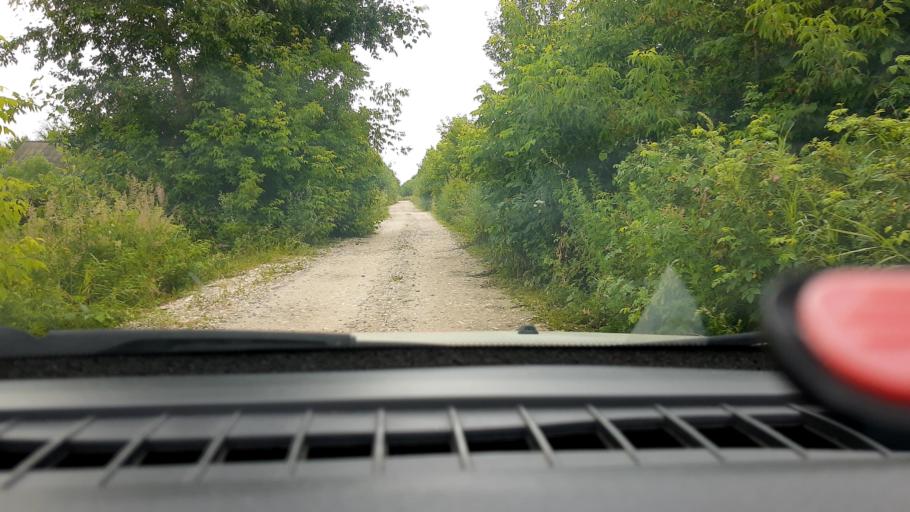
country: RU
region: Vladimir
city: Luknovo
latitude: 56.2239
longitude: 42.0263
